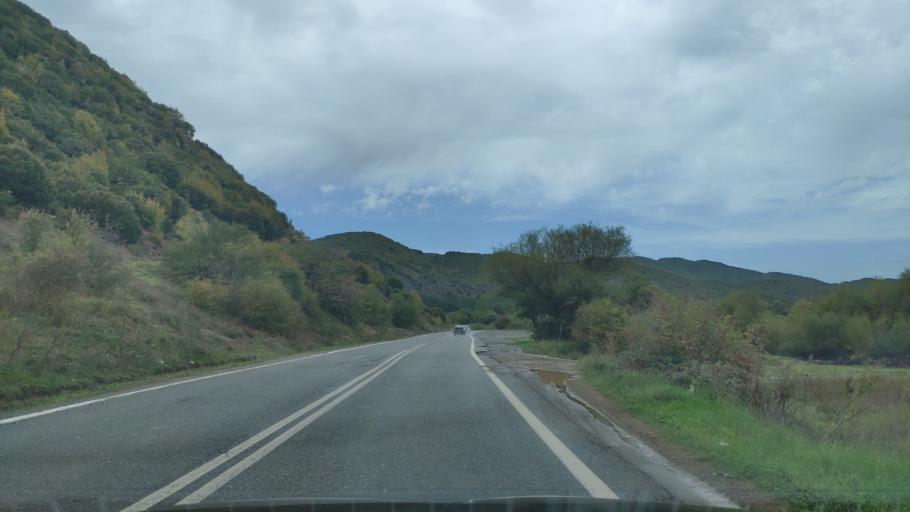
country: GR
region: Peloponnese
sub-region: Nomos Arkadias
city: Dimitsana
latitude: 37.6279
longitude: 22.0695
